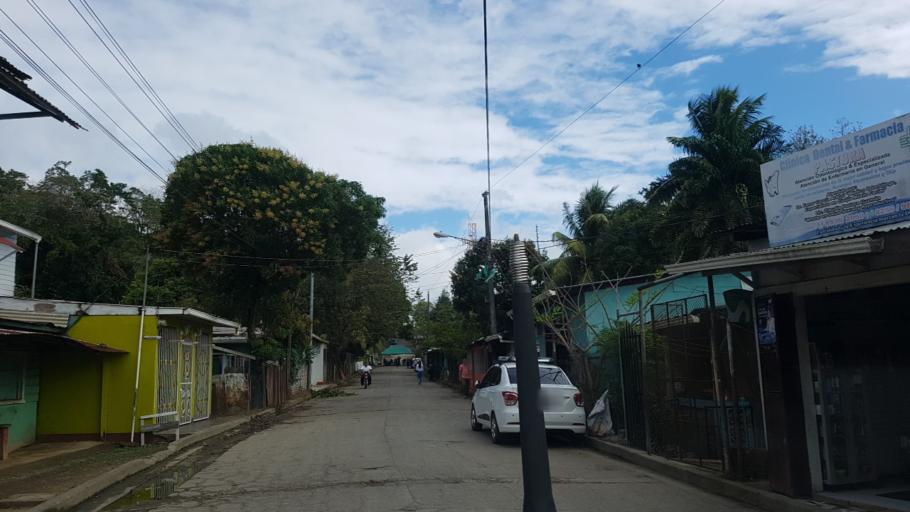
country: NI
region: Atlantico Norte (RAAN)
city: Siuna
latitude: 13.7405
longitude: -84.7817
